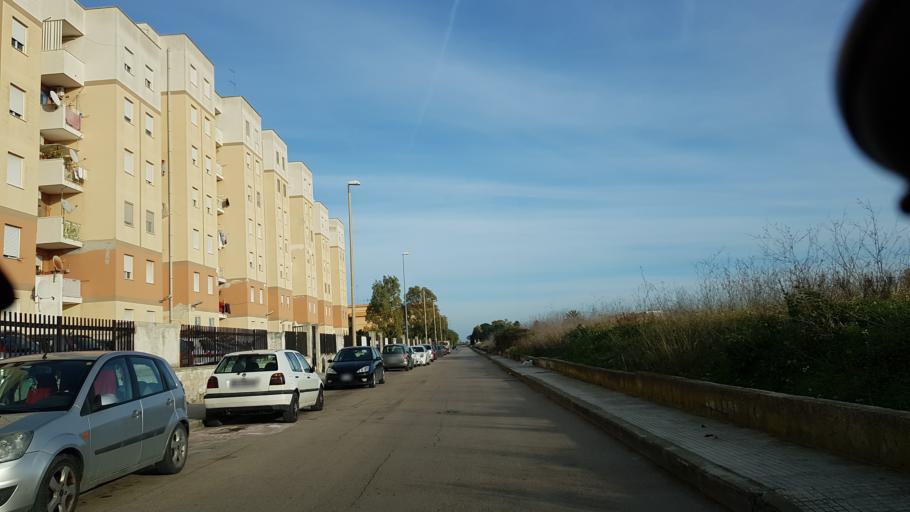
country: IT
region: Apulia
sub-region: Provincia di Brindisi
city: Brindisi
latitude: 40.6167
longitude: 17.9206
